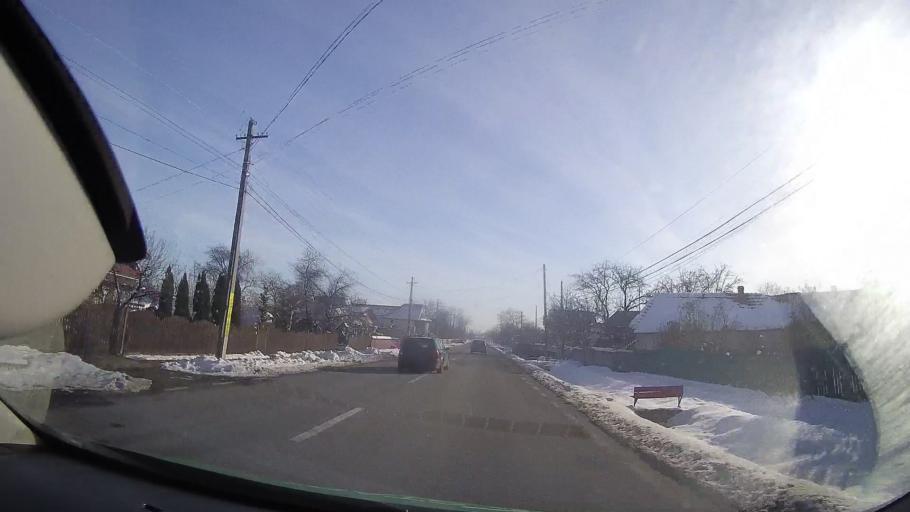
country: RO
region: Neamt
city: Bodesti
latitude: 47.0346
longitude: 26.4128
